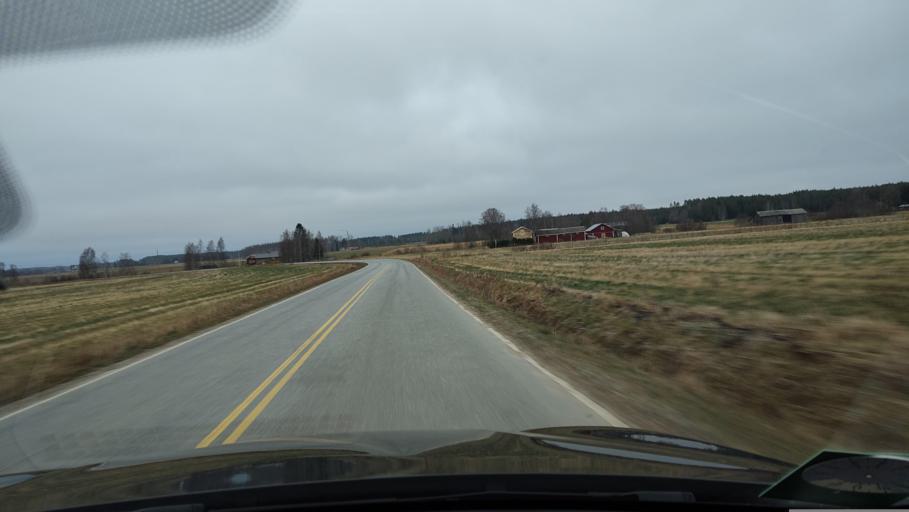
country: FI
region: Southern Ostrobothnia
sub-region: Suupohja
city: Karijoki
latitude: 62.2680
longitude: 21.7241
